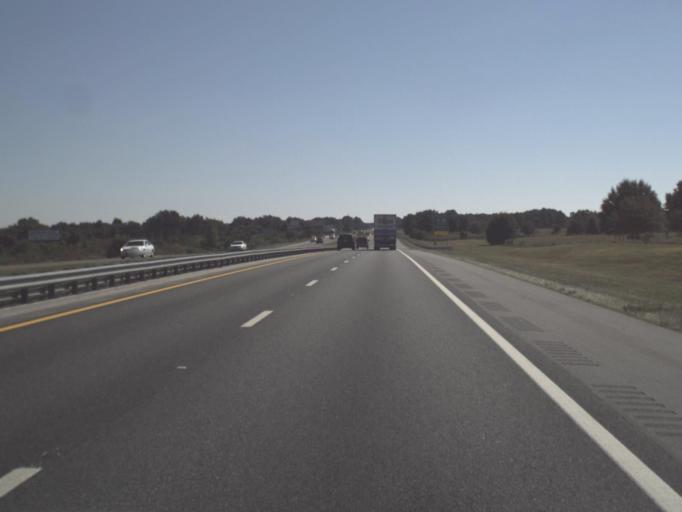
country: US
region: Florida
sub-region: Lake County
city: Hawthorne
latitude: 28.7031
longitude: -81.8839
